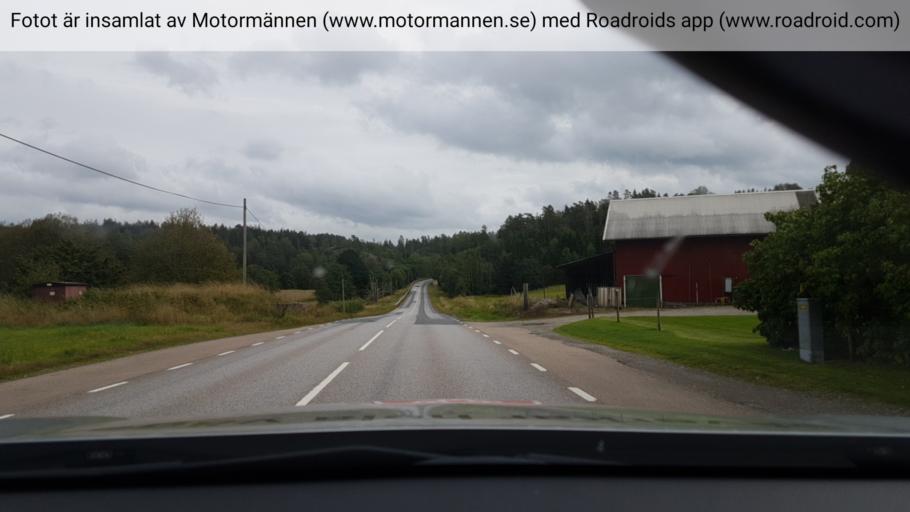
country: SE
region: Vaestra Goetaland
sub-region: Sotenas Kommun
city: Hunnebostrand
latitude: 58.5618
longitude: 11.3956
